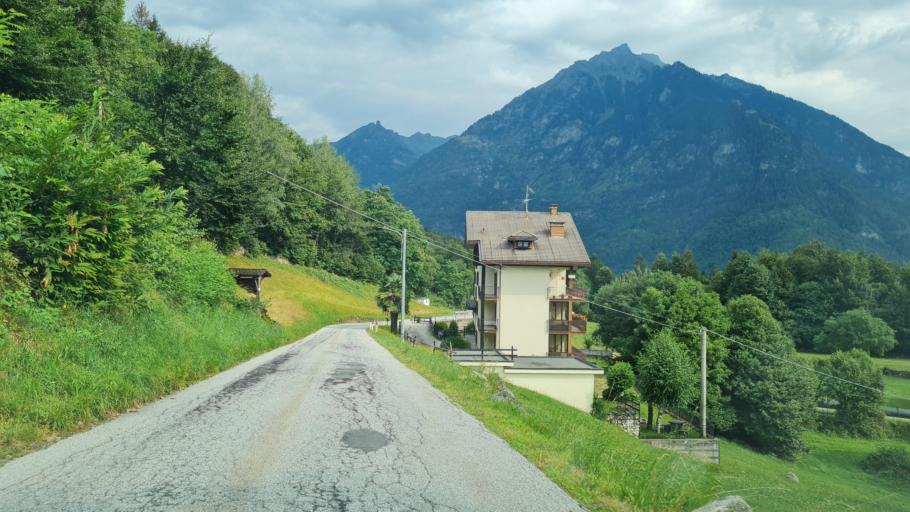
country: IT
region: Piedmont
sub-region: Provincia Verbano-Cusio-Ossola
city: Baceno
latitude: 46.2434
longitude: 8.3144
